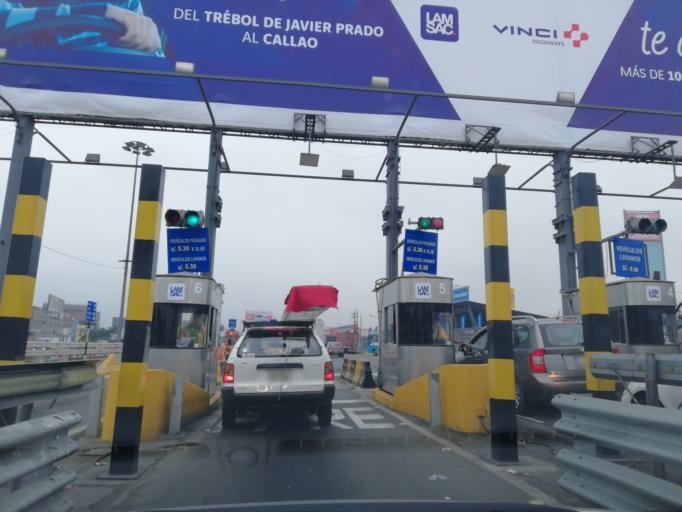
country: PE
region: Lima
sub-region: Lima
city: San Luis
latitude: -12.0671
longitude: -76.9715
